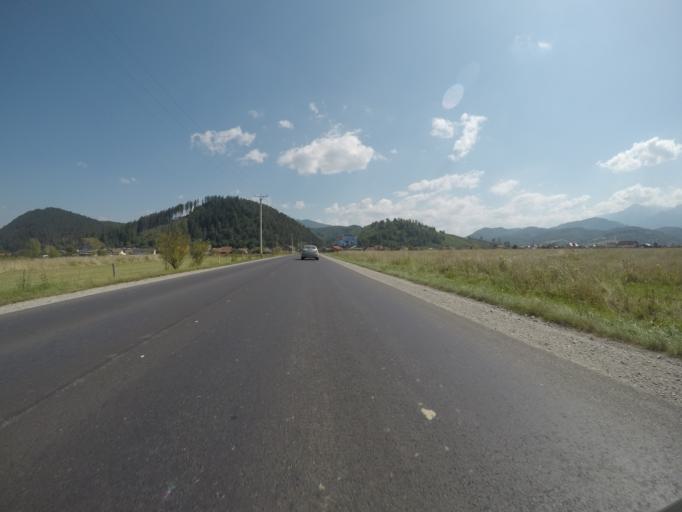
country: RO
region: Brasov
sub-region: Oras Rasnov
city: Rasnov
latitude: 45.5783
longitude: 25.4516
